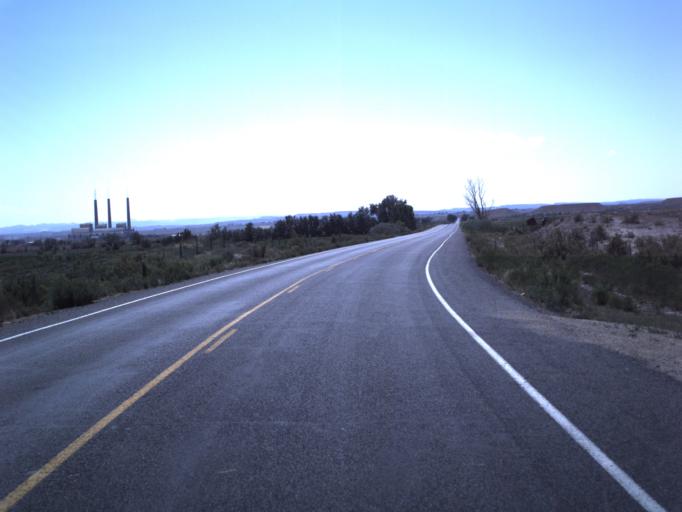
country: US
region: Utah
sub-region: Emery County
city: Orangeville
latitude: 39.2095
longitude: -111.0481
